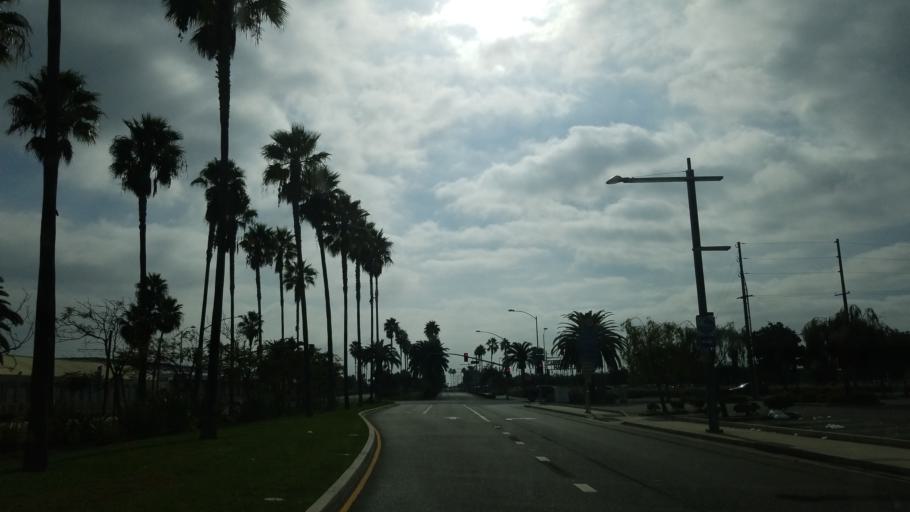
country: US
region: California
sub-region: Los Angeles County
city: San Pedro
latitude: 33.7270
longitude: -118.2786
